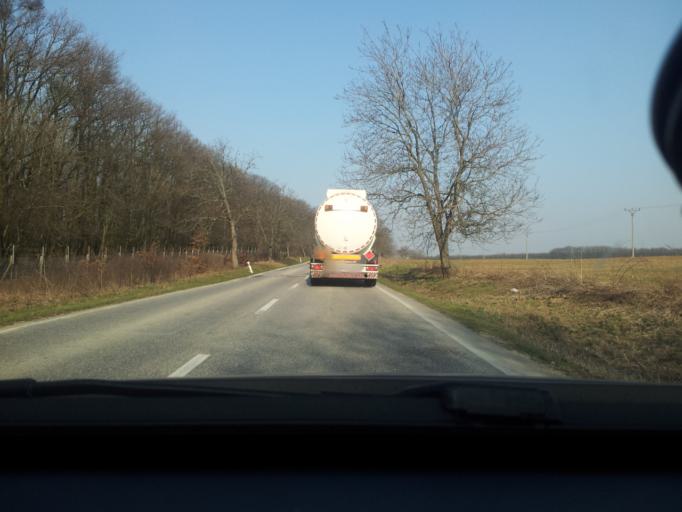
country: SK
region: Nitriansky
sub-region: Okres Nitra
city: Nitra
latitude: 48.3352
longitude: 18.0001
